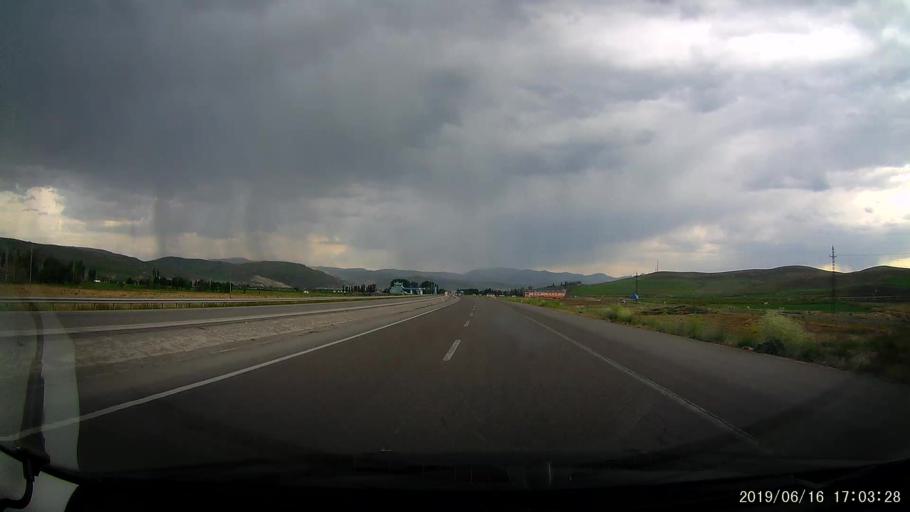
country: TR
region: Erzurum
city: Askale
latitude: 39.9366
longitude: 40.7311
